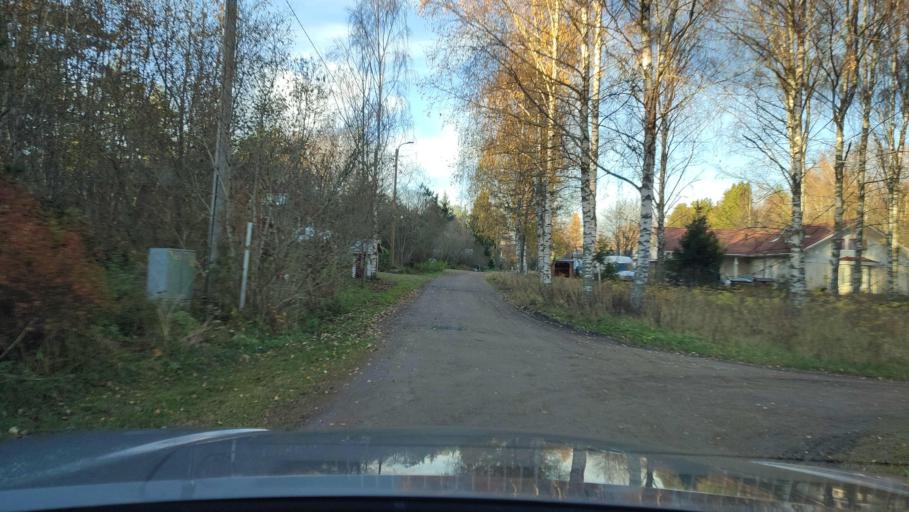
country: FI
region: Ostrobothnia
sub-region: Vaasa
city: Teeriniemi
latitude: 63.0681
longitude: 21.6954
